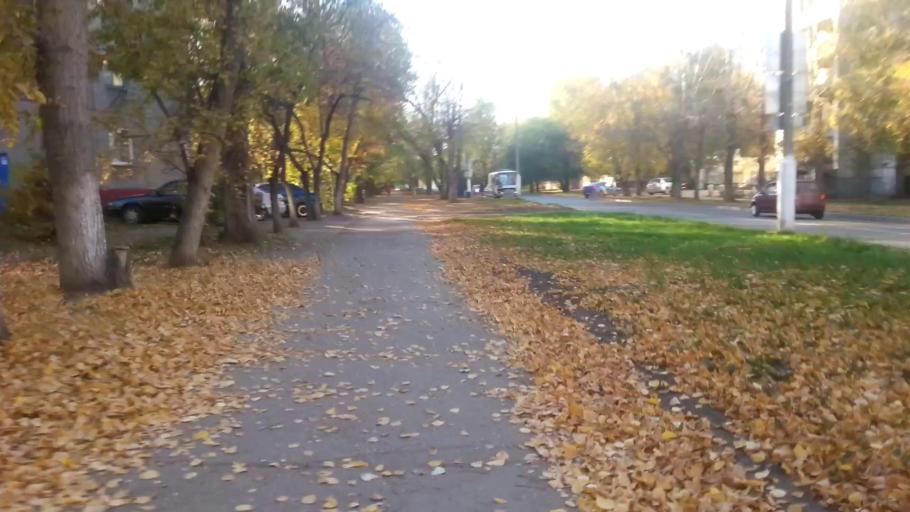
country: RU
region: Altai Krai
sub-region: Gorod Barnaulskiy
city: Barnaul
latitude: 53.3645
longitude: 83.6991
